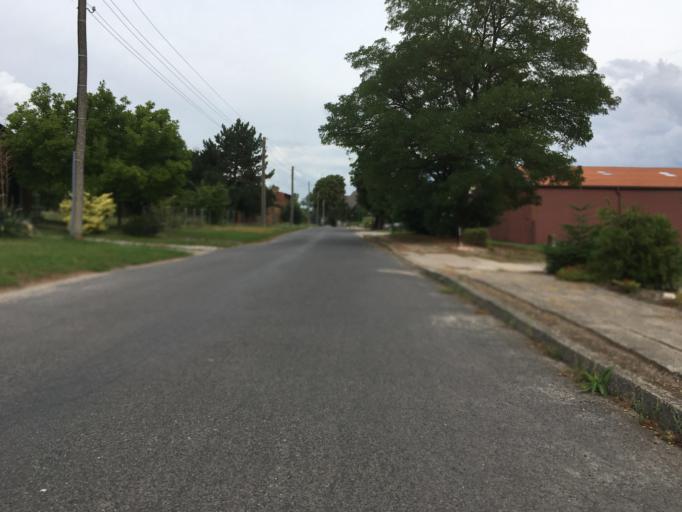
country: DE
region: Brandenburg
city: Prenzlau
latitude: 53.2619
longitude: 13.8488
